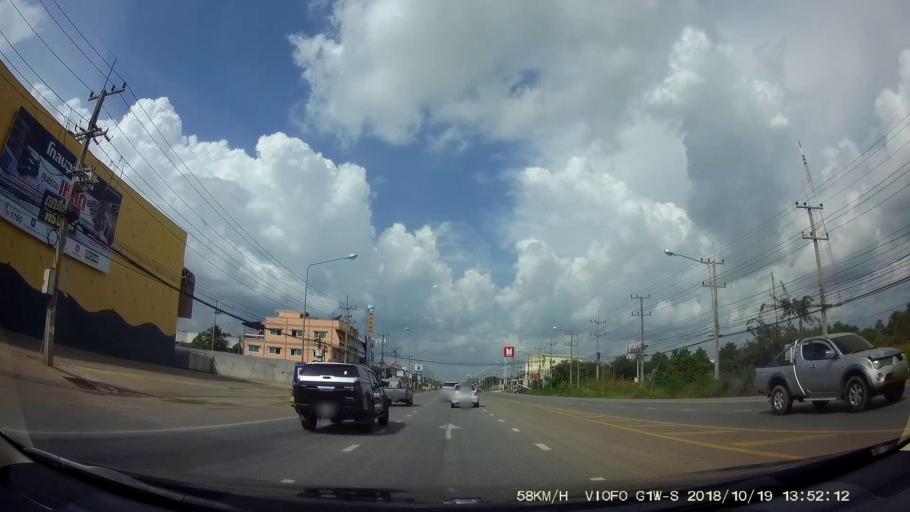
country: TH
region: Chaiyaphum
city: Chaiyaphum
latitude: 15.7644
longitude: 102.0249
